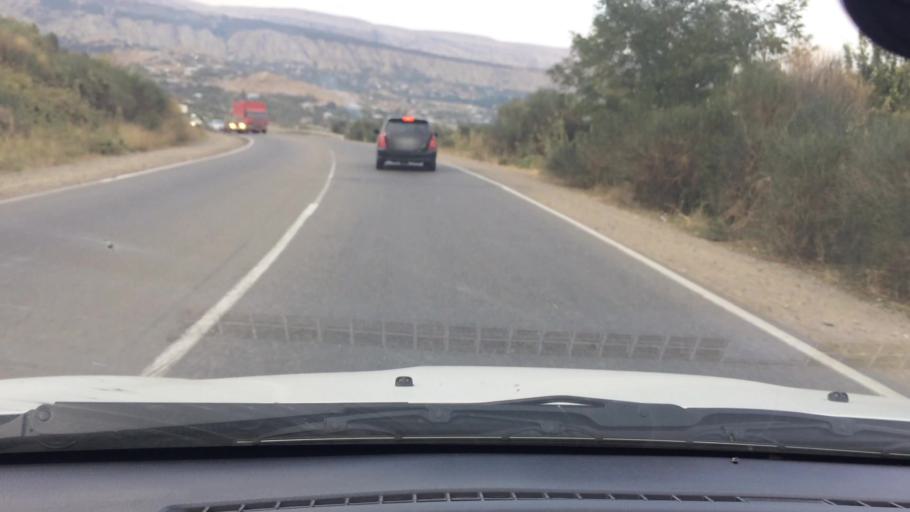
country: GE
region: T'bilisi
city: Tbilisi
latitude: 41.5934
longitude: 44.7805
